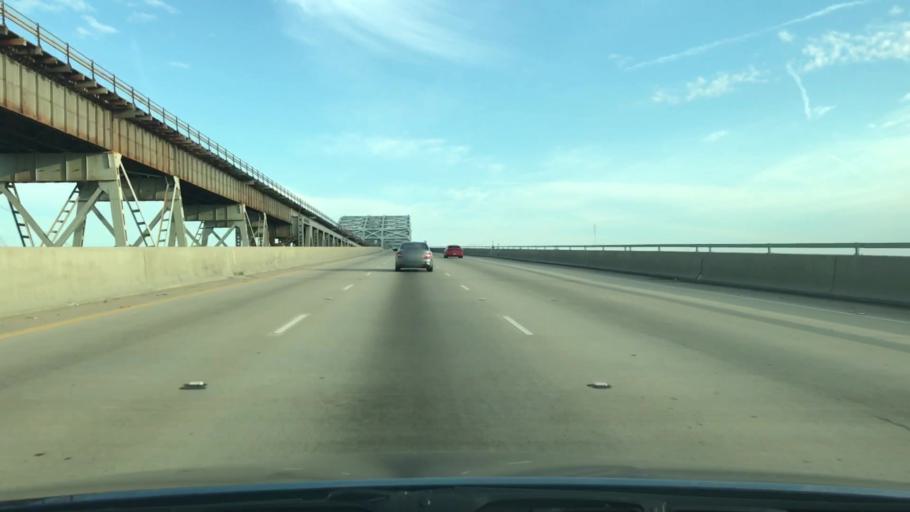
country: US
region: Louisiana
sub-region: Jefferson Parish
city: Bridge City
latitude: 29.9492
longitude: -90.1749
